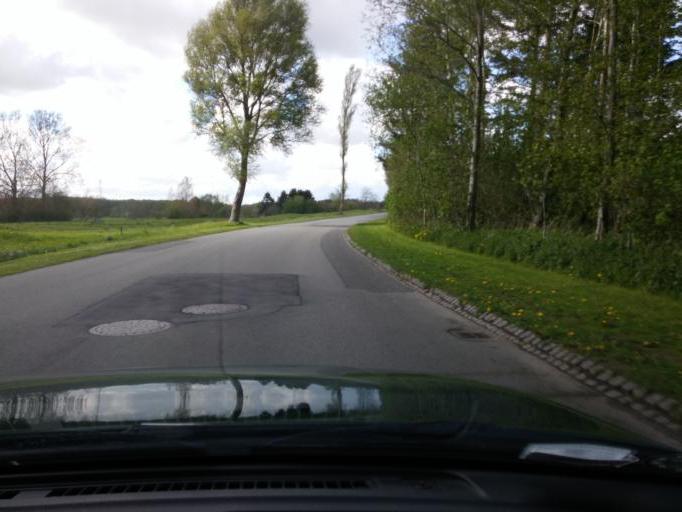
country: DK
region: South Denmark
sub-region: Faaborg-Midtfyn Kommune
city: Ringe
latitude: 55.2332
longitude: 10.5273
